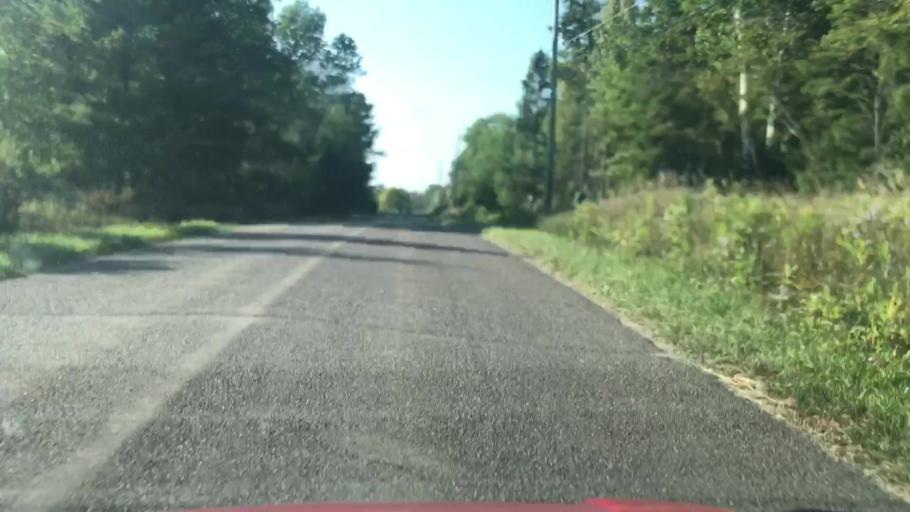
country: US
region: Michigan
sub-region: Chippewa County
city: Sault Ste. Marie
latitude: 46.2885
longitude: -84.0610
